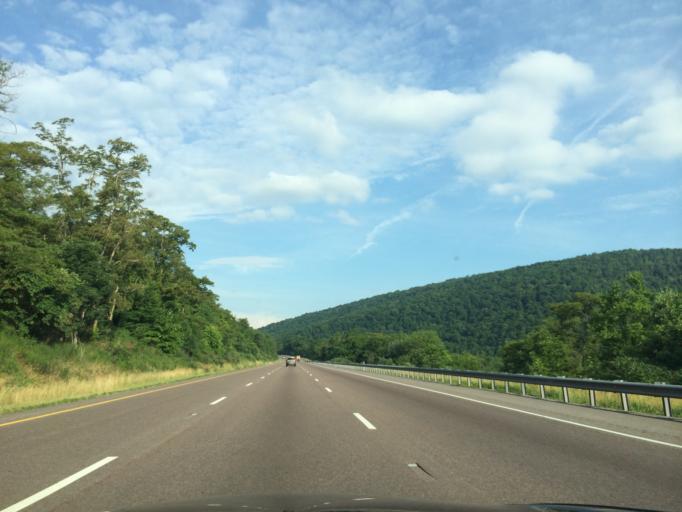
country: US
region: Maryland
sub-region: Allegany County
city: La Vale
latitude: 39.6400
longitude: -78.8645
